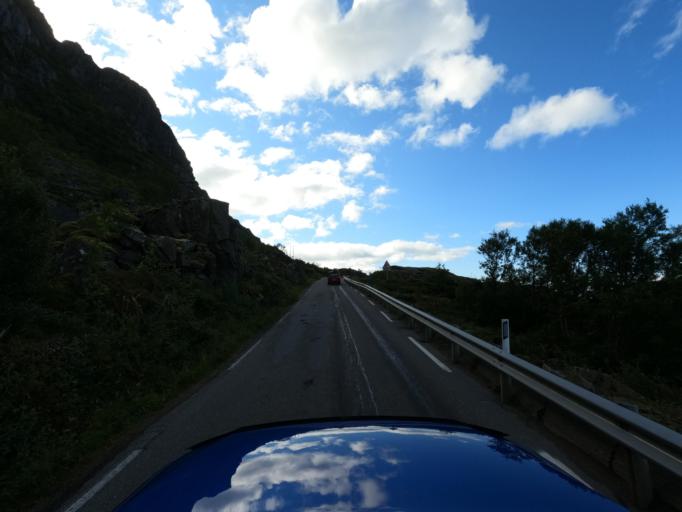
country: NO
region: Nordland
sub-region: Vagan
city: Kabelvag
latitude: 68.1795
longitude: 14.2130
